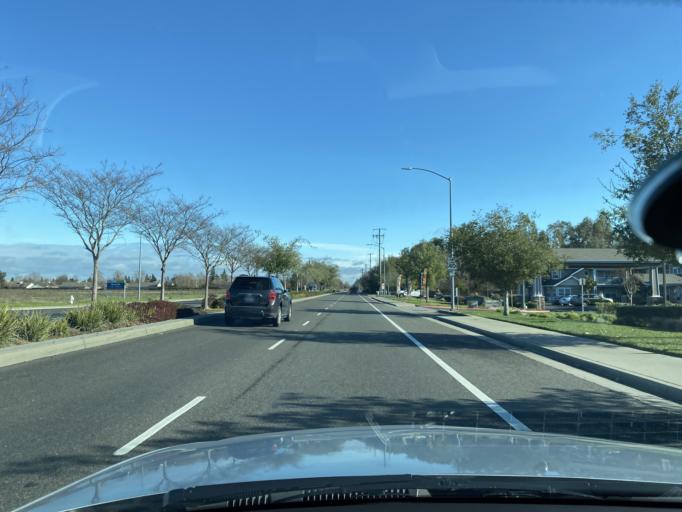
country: US
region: California
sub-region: Sacramento County
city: Elk Grove
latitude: 38.4380
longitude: -121.3920
